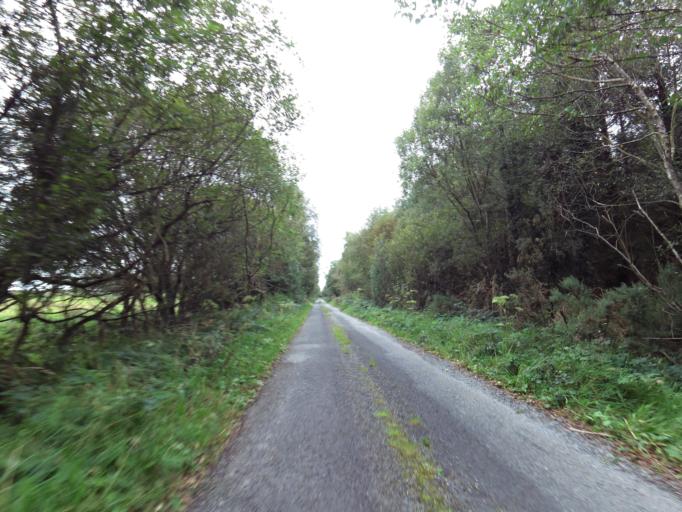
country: IE
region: Leinster
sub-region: Uibh Fhaili
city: Ferbane
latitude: 53.2466
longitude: -7.7397
